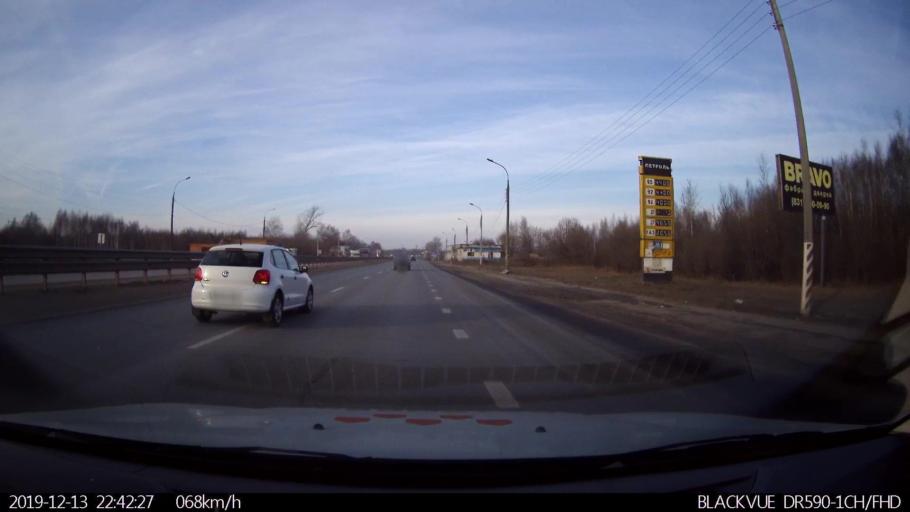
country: RU
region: Nizjnij Novgorod
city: Kstovo
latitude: 56.1897
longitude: 44.1352
